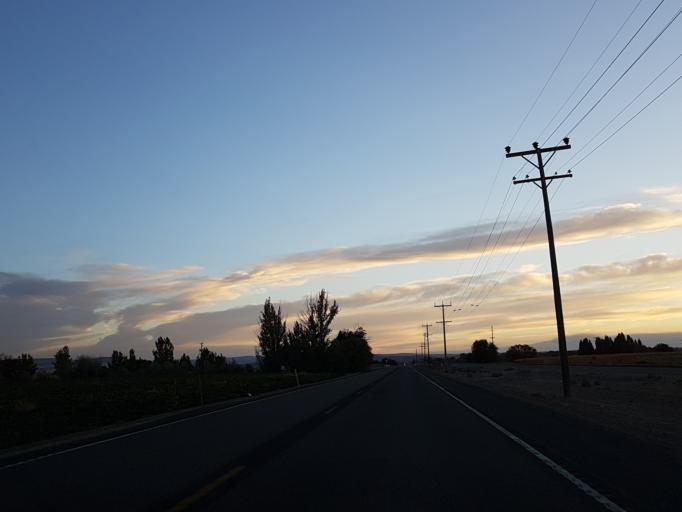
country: US
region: Oregon
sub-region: Malheur County
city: Vale
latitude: 43.9698
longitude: -117.2689
